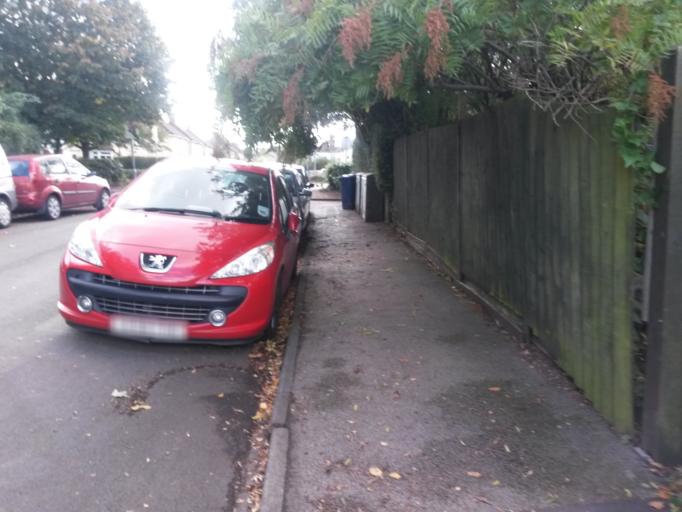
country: GB
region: England
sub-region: Cambridgeshire
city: Cambridge
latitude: 52.2194
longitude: 0.1178
